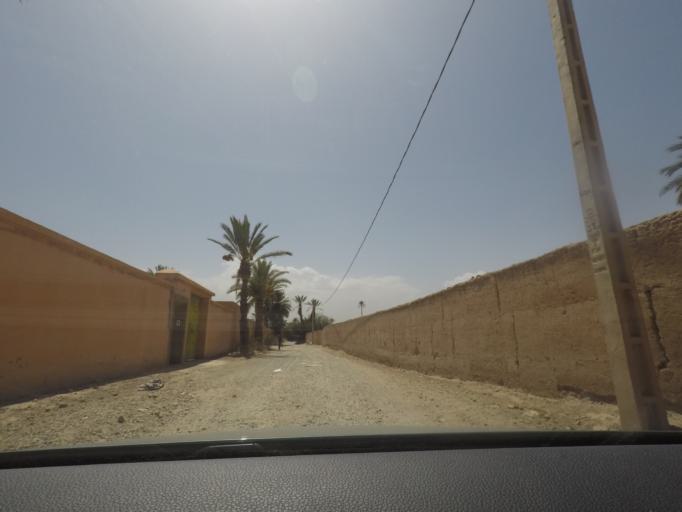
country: MA
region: Marrakech-Tensift-Al Haouz
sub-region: Marrakech
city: Marrakesh
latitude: 31.5818
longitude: -8.0287
